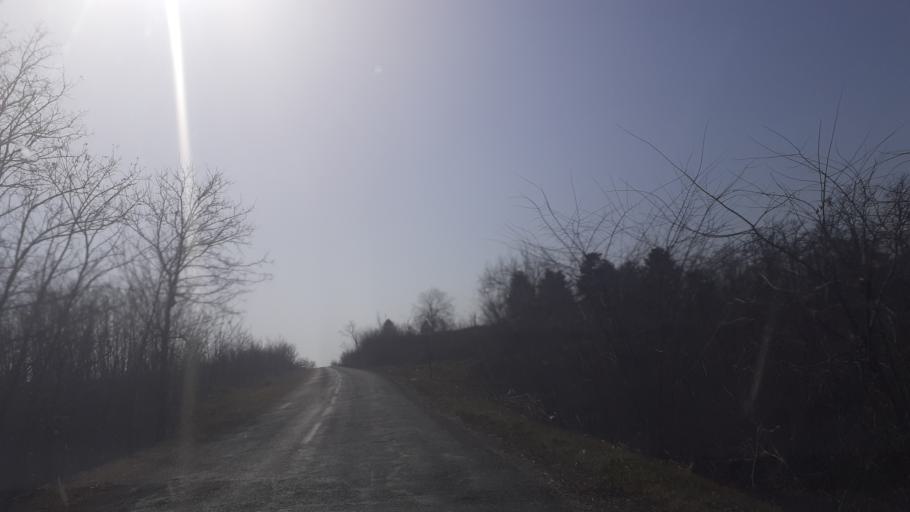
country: HU
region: Pest
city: Dabas
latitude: 47.1482
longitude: 19.3293
